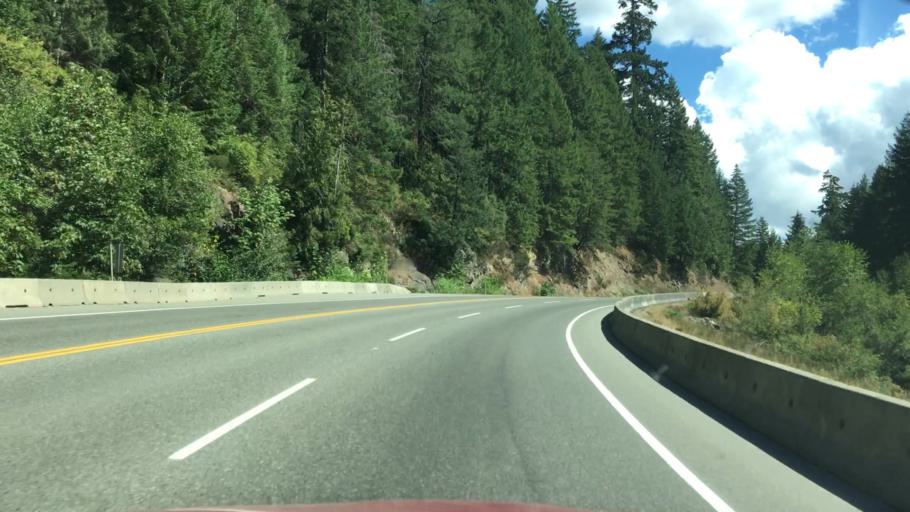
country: CA
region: British Columbia
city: Port Alberni
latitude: 49.2664
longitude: -124.7323
